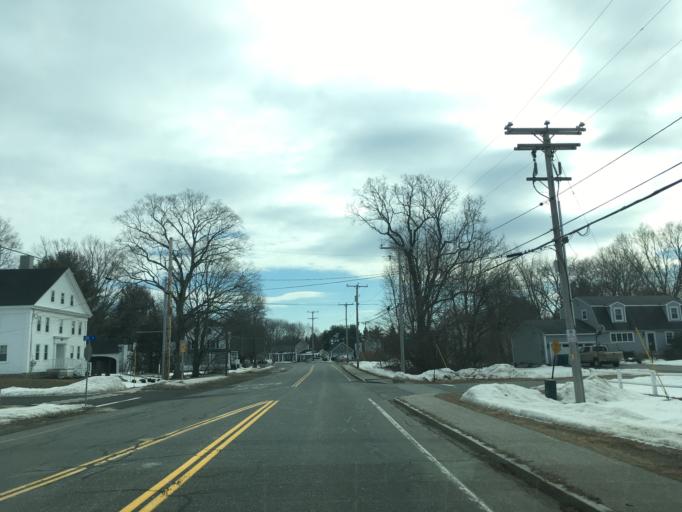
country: US
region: New Hampshire
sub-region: Rockingham County
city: Hampton
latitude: 42.9328
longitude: -70.8280
